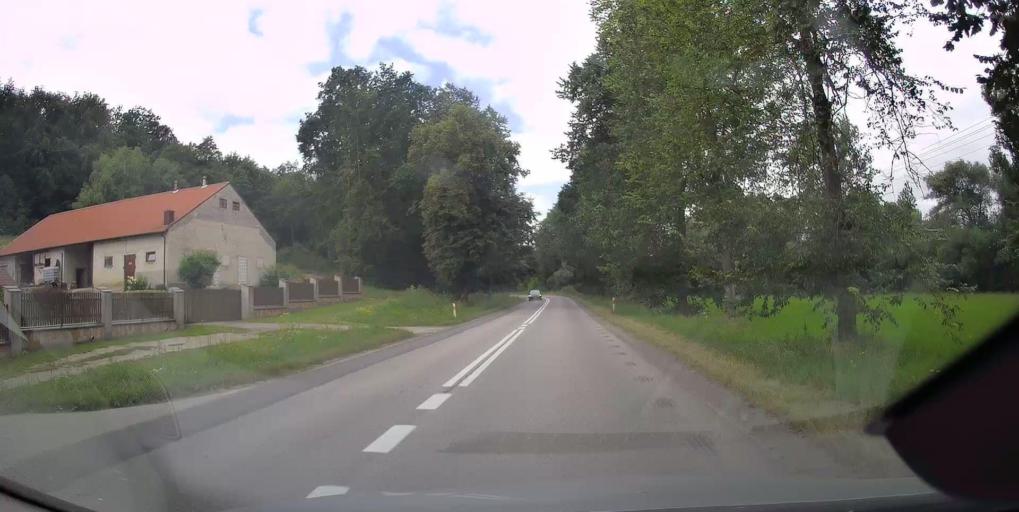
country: PL
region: Swietokrzyskie
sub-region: Powiat sandomierski
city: Klimontow
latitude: 50.6583
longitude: 21.4340
